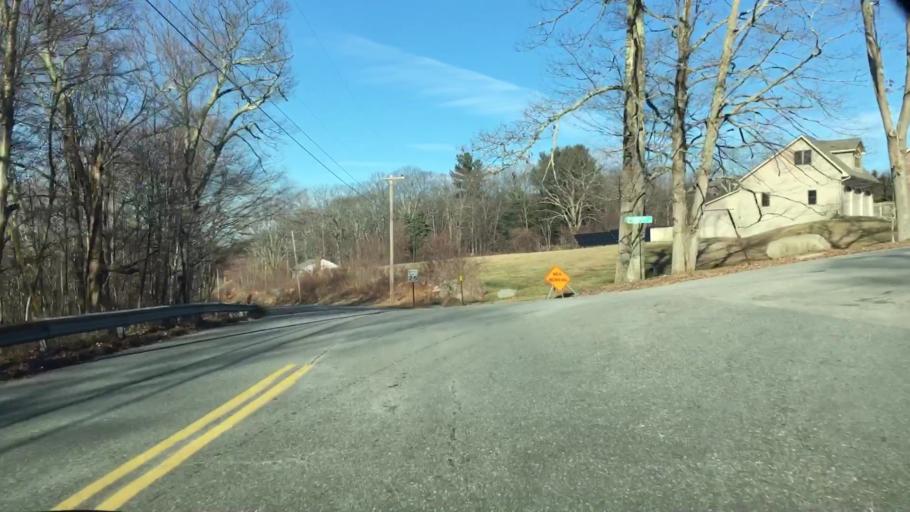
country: US
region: Connecticut
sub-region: Tolland County
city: Tolland
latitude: 41.8892
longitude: -72.3865
